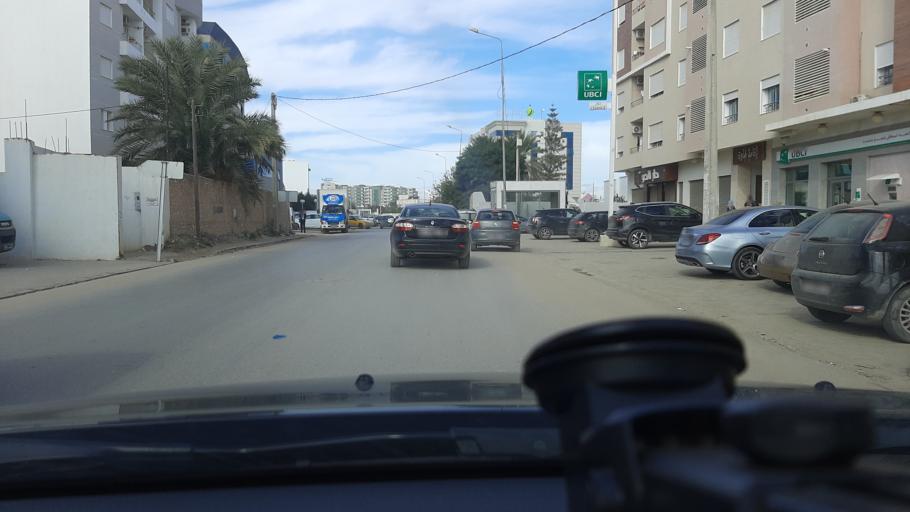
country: TN
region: Safaqis
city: Sfax
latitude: 34.7577
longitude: 10.7339
